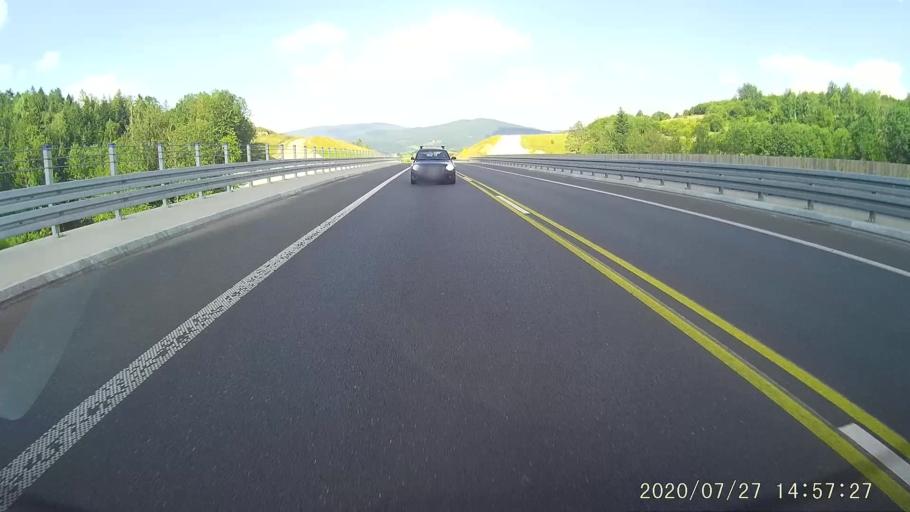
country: PL
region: Lesser Poland Voivodeship
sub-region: Powiat myslenicki
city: Lubien
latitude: 49.6981
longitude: 19.9406
